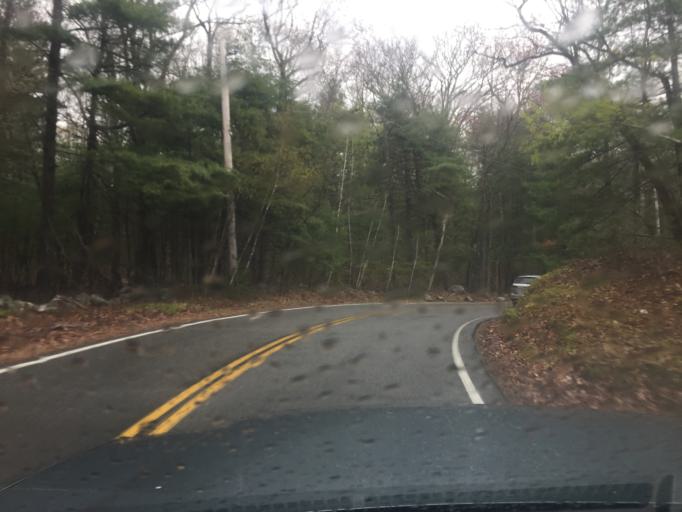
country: US
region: Massachusetts
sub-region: Norfolk County
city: Westwood
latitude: 42.2288
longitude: -71.2456
